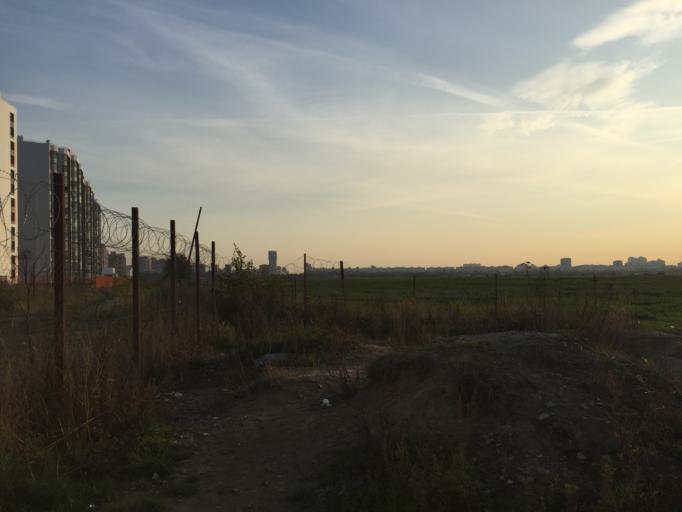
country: RU
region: Leningrad
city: Bugry
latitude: 60.0608
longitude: 30.4153
